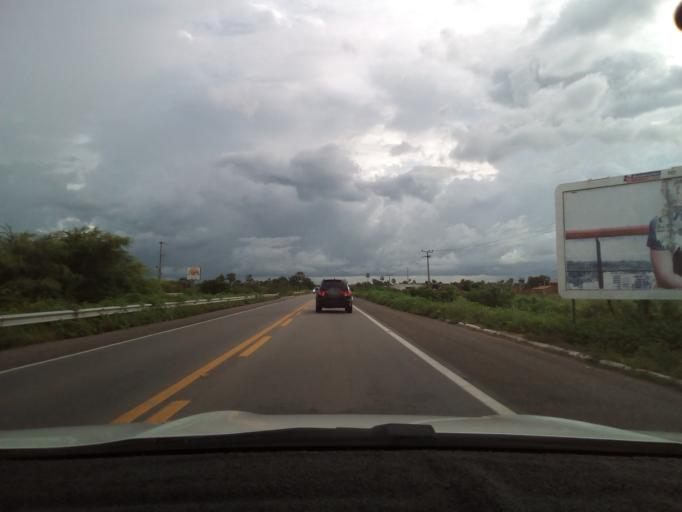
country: BR
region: Ceara
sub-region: Aracati
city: Aracati
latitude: -4.5753
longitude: -37.7658
